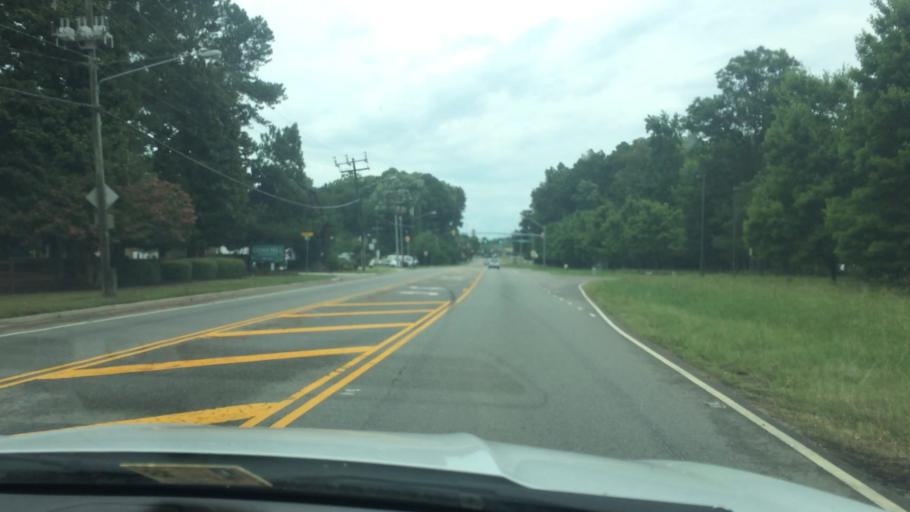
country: US
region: Virginia
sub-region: York County
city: Yorktown
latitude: 37.1845
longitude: -76.5719
